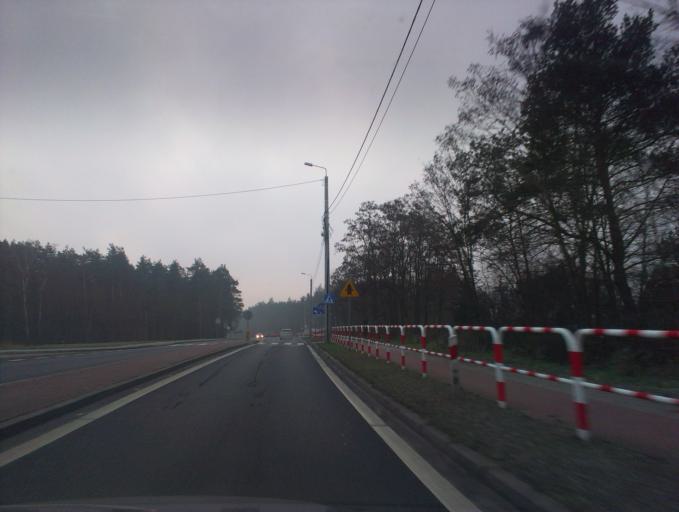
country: PL
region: Greater Poland Voivodeship
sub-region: Powiat chodzieski
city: Chodziez
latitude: 52.9758
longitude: 16.9286
